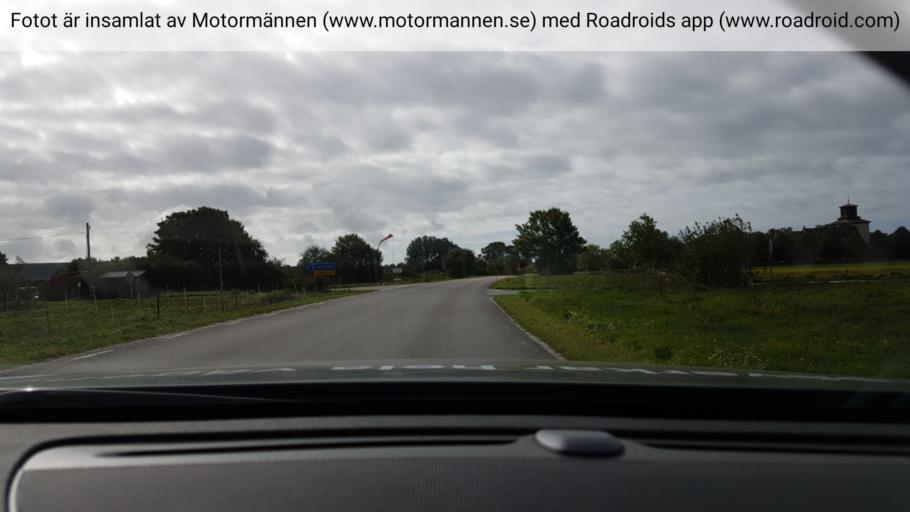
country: SE
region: Gotland
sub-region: Gotland
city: Hemse
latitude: 56.9728
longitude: 18.2351
